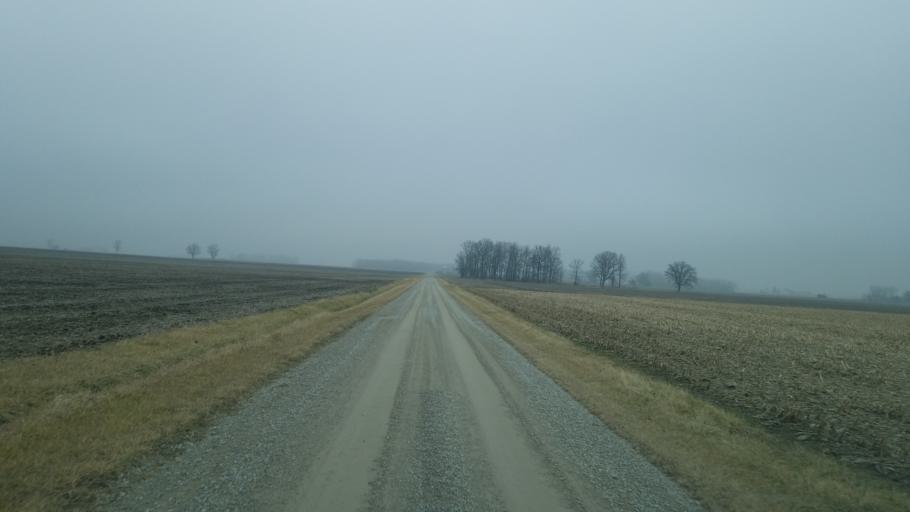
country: US
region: Indiana
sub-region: Adams County
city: Geneva
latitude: 40.6321
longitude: -85.0699
